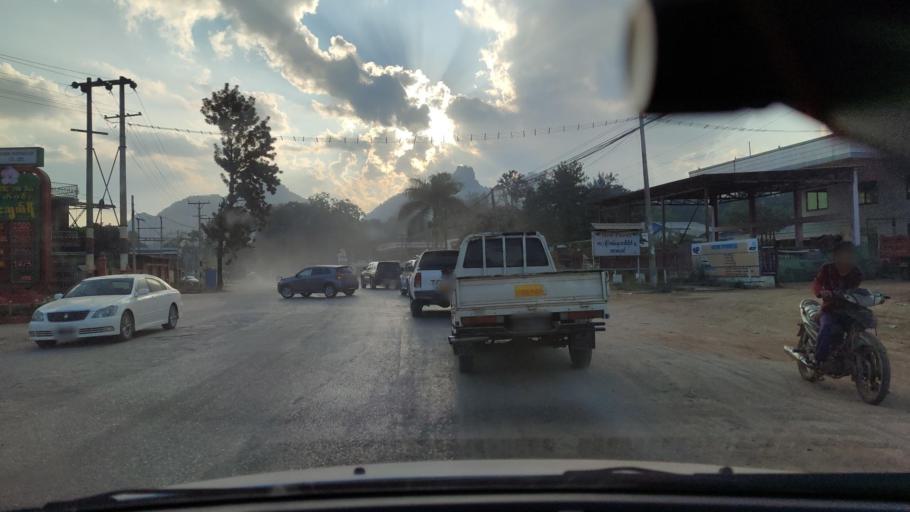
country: MM
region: Shan
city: Lashio
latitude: 22.9287
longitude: 97.7290
